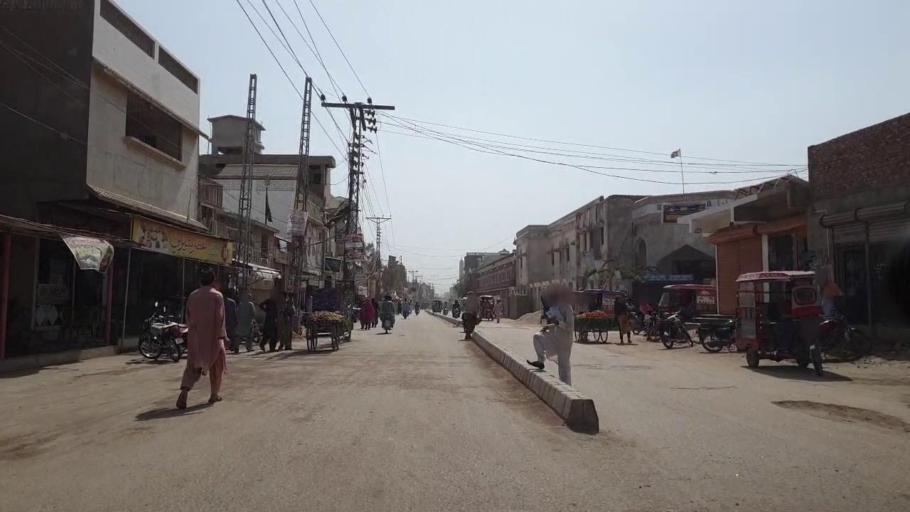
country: PK
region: Sindh
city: Matli
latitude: 25.0452
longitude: 68.6560
